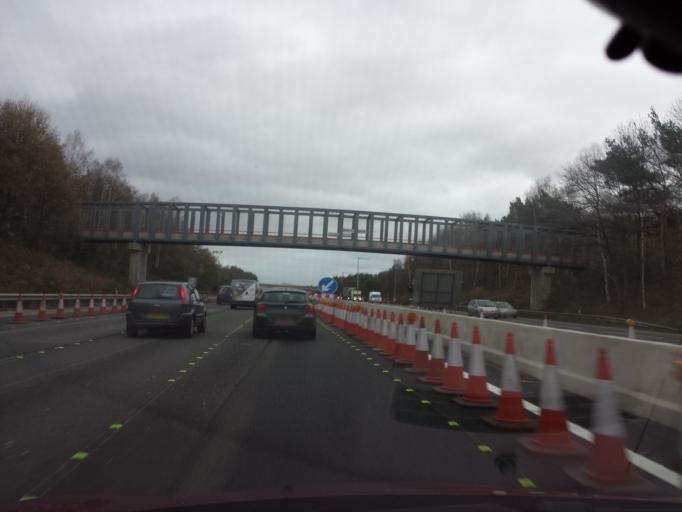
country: GB
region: England
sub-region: Surrey
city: Chobham
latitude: 51.3699
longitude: -0.6218
